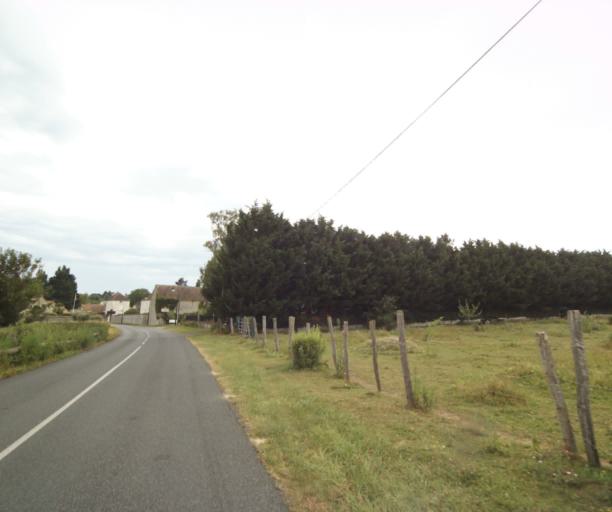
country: FR
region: Ile-de-France
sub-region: Departement de Seine-et-Marne
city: Saint-Sauveur-sur-Ecole
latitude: 48.4918
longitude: 2.5433
